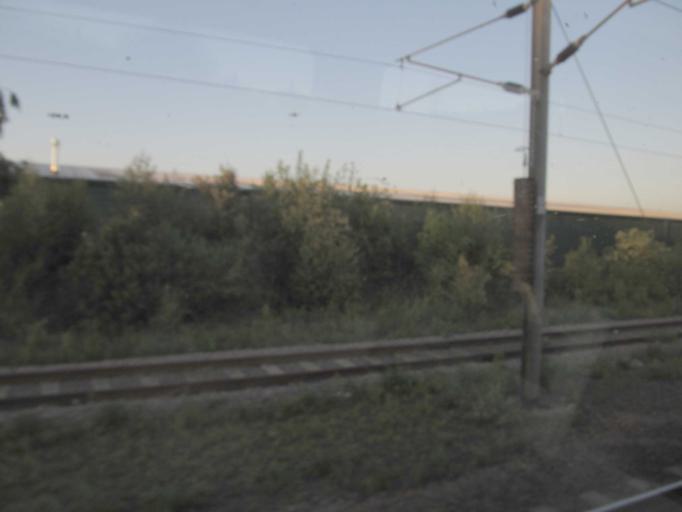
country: GB
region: England
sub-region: Lincolnshire
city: Grantham
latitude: 52.9021
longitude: -0.6369
